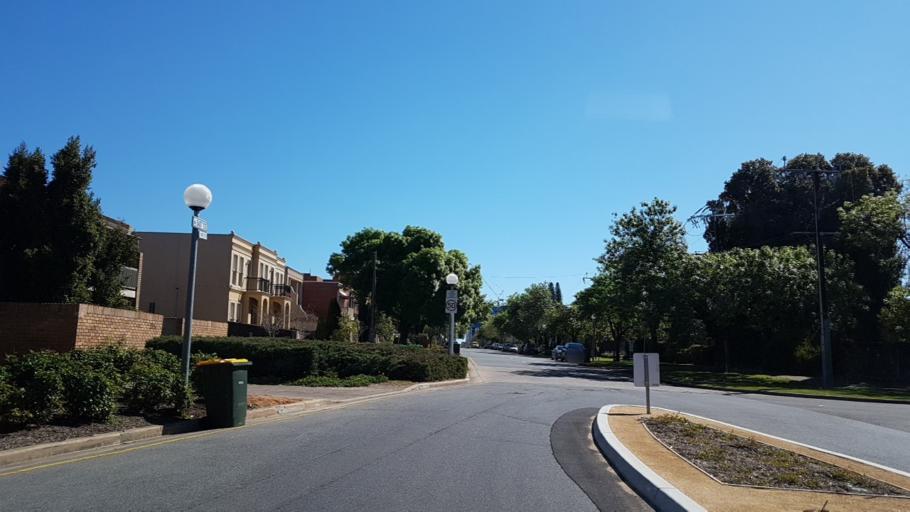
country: AU
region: South Australia
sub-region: Adelaide
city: Adelaide
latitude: -34.9293
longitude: 138.6158
